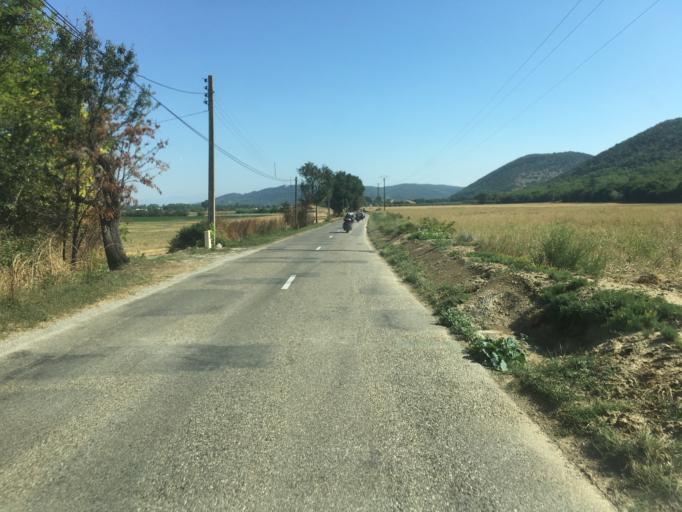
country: FR
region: Provence-Alpes-Cote d'Azur
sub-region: Departement des Alpes-de-Haute-Provence
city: Villeneuve
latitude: 43.8617
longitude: 5.8923
